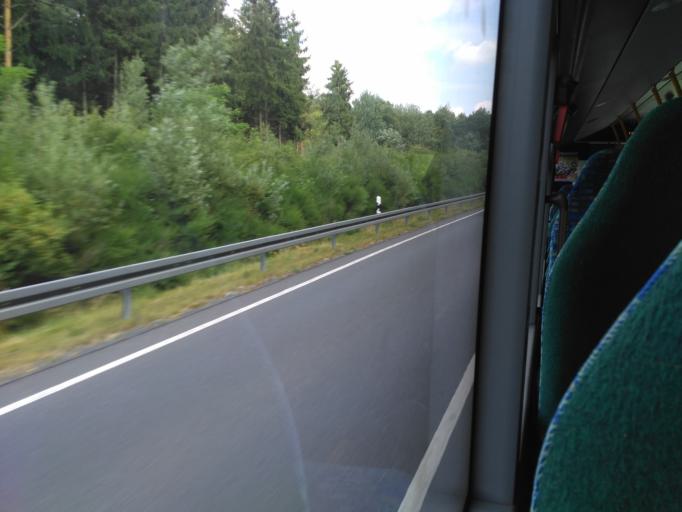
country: DE
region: Saxony
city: Moritzburg
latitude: 51.1593
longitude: 13.6285
